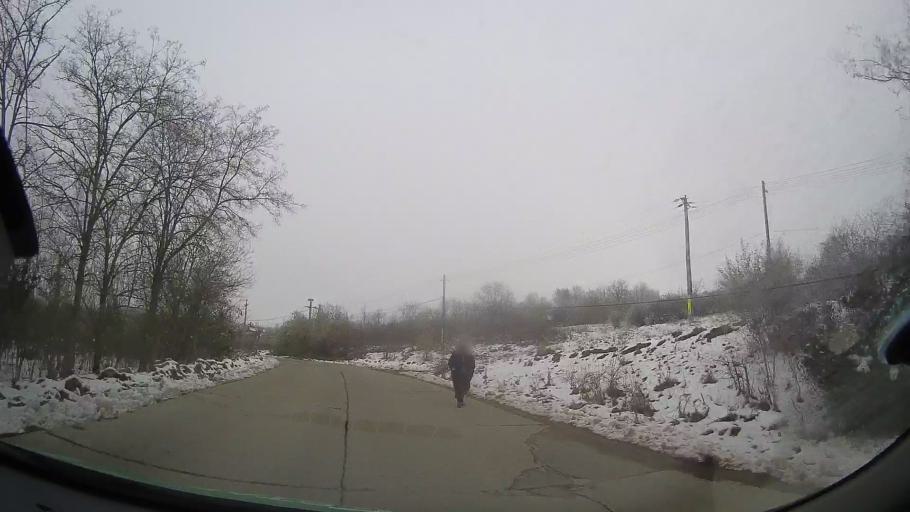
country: RO
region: Vrancea
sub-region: Comuna Boghesti
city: Boghesti
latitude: 46.2063
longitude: 27.4415
